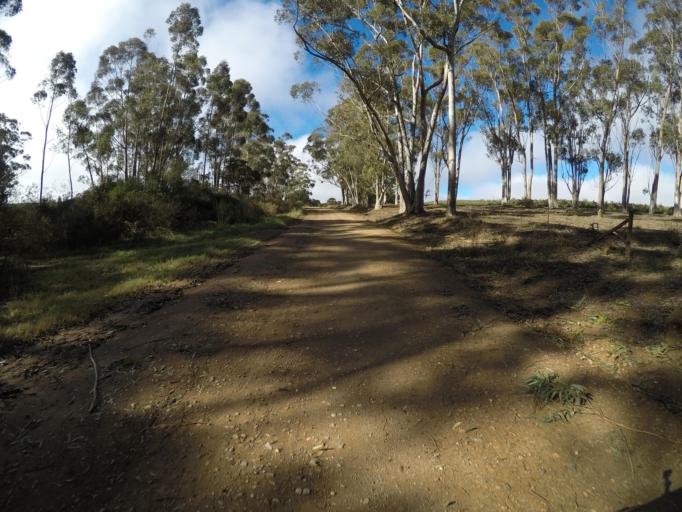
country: ZA
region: Western Cape
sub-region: Cape Winelands District Municipality
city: Ashton
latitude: -34.1123
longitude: 19.8005
